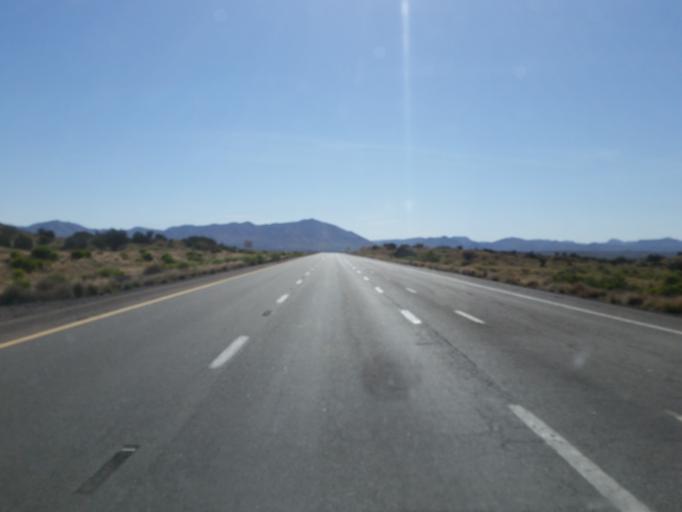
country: US
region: Arizona
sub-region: Mohave County
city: New Kingman-Butler
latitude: 35.1593
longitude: -113.6919
